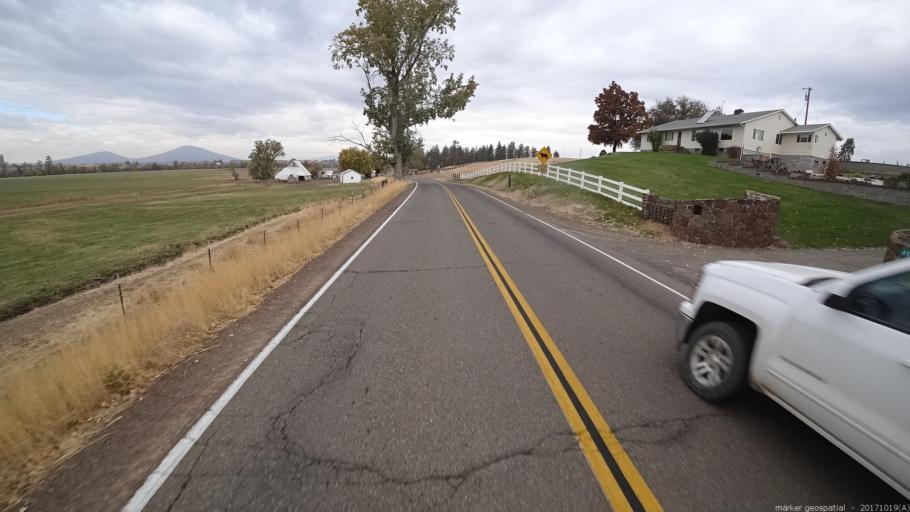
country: US
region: California
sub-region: Shasta County
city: Burney
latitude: 41.0534
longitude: -121.3564
